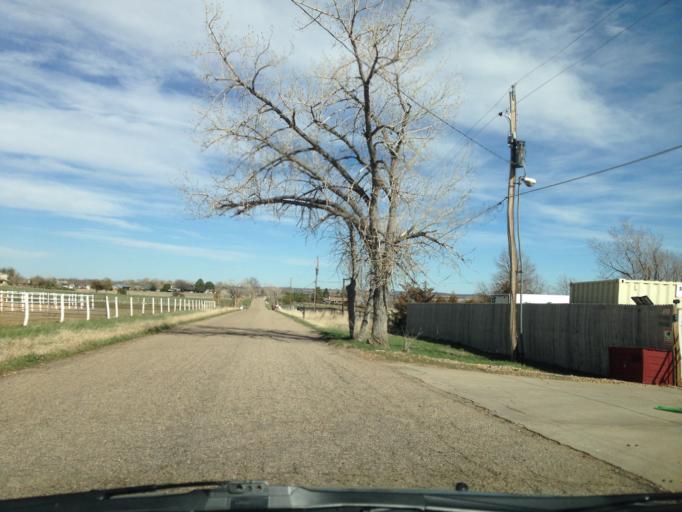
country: US
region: Colorado
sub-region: Boulder County
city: Gunbarrel
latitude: 40.0618
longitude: -105.1306
